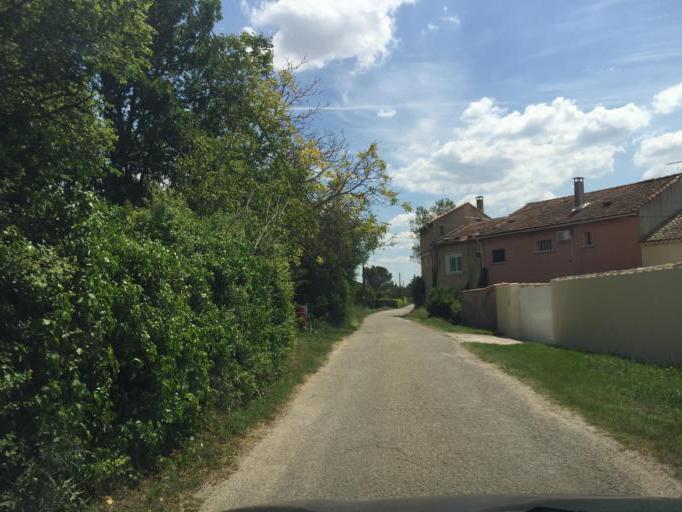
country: FR
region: Provence-Alpes-Cote d'Azur
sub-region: Departement du Vaucluse
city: Jonquieres
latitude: 44.1283
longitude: 4.8932
